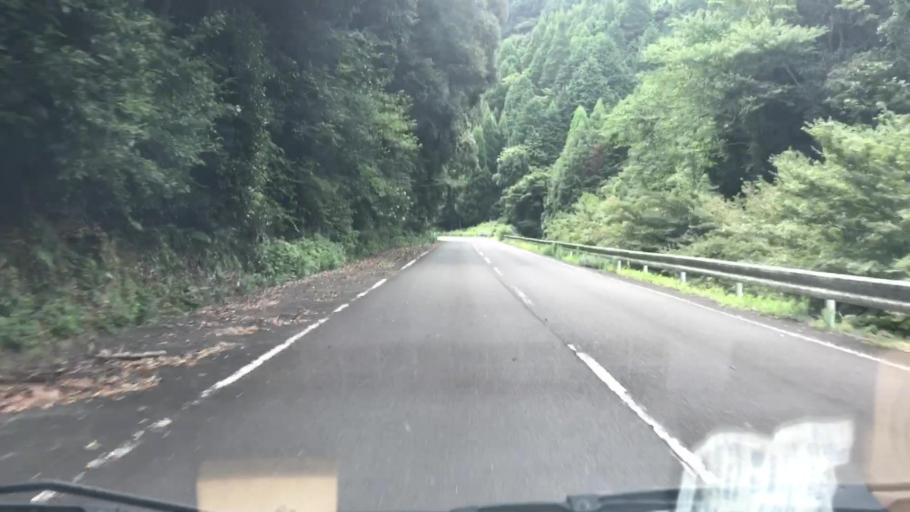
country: JP
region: Saga Prefecture
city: Takeocho-takeo
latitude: 33.2266
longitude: 130.0045
